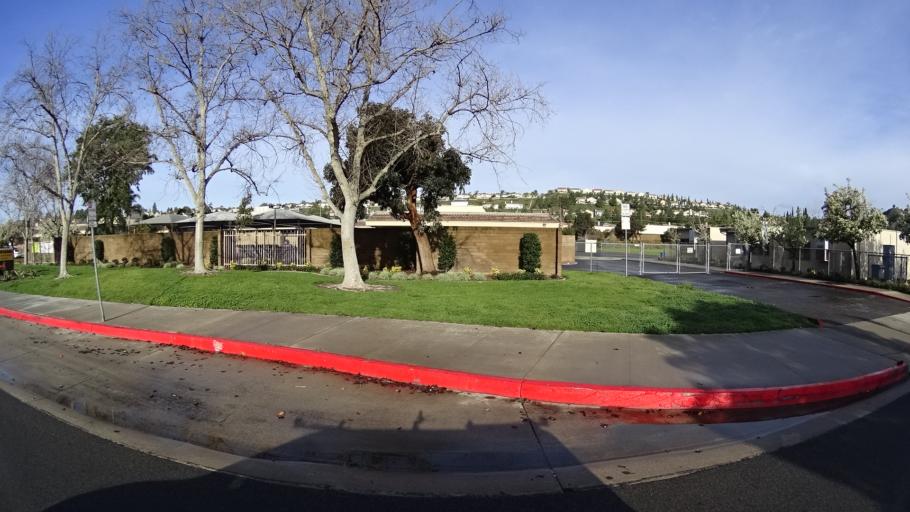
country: US
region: California
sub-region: Orange County
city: Yorba Linda
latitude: 33.8682
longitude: -117.7727
